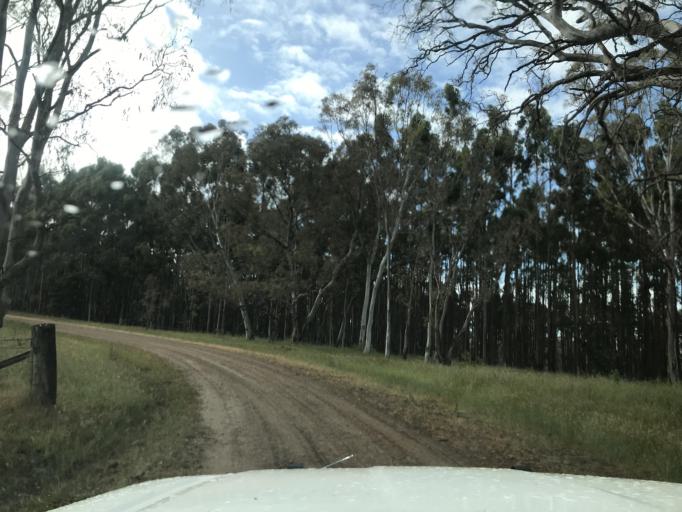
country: AU
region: South Australia
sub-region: Wattle Range
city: Penola
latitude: -37.2200
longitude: 141.2861
